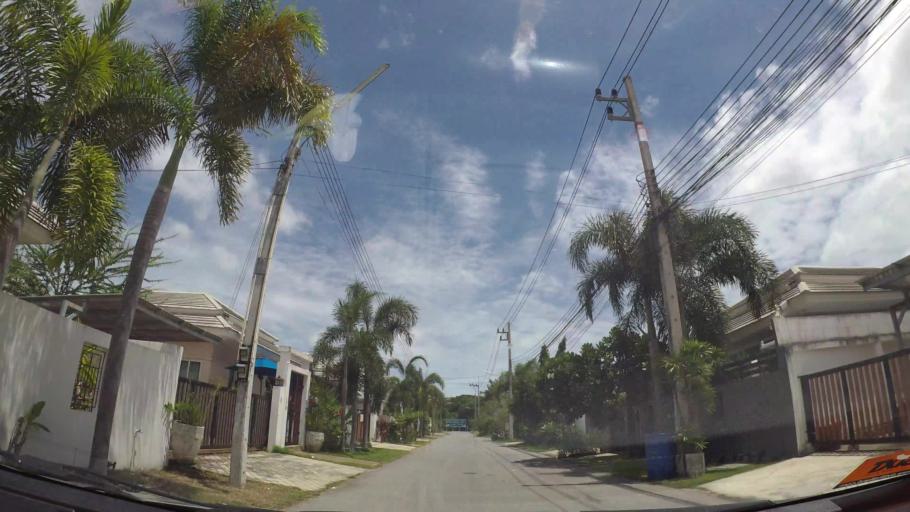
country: TH
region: Chon Buri
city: Sattahip
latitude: 12.7422
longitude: 100.8911
